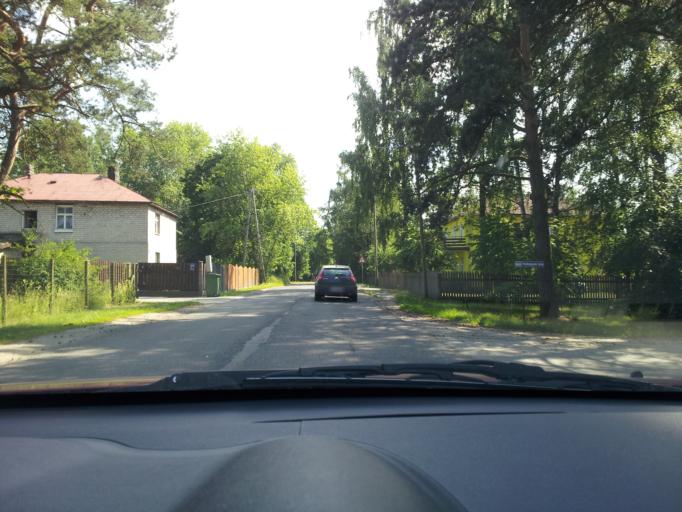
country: LV
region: Riga
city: Bolderaja
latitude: 57.0538
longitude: 24.0723
